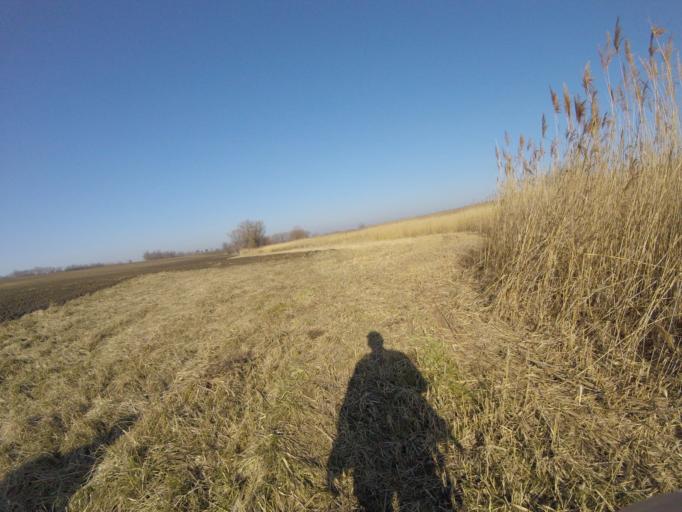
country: HU
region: Komarom-Esztergom
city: Csaszar
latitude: 47.5329
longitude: 18.1897
